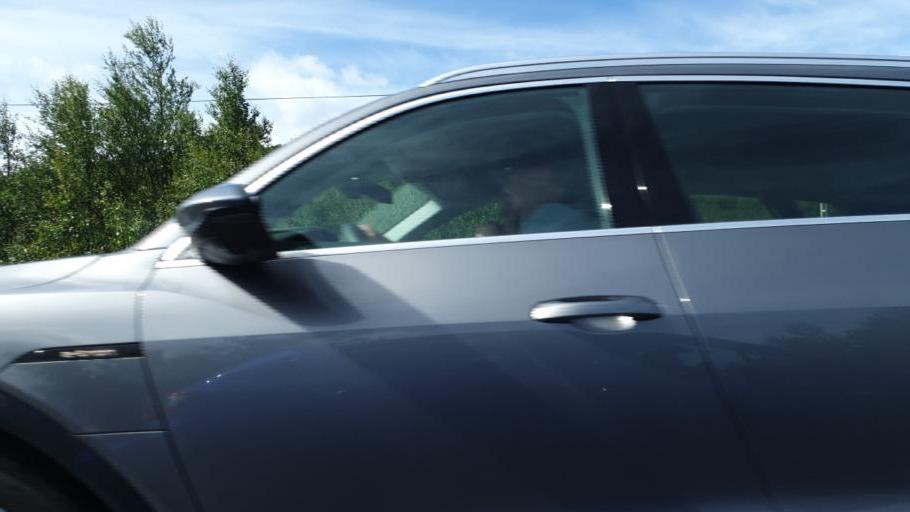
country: NO
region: Oppland
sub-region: Oystre Slidre
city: Heggenes
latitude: 61.5003
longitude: 8.8425
